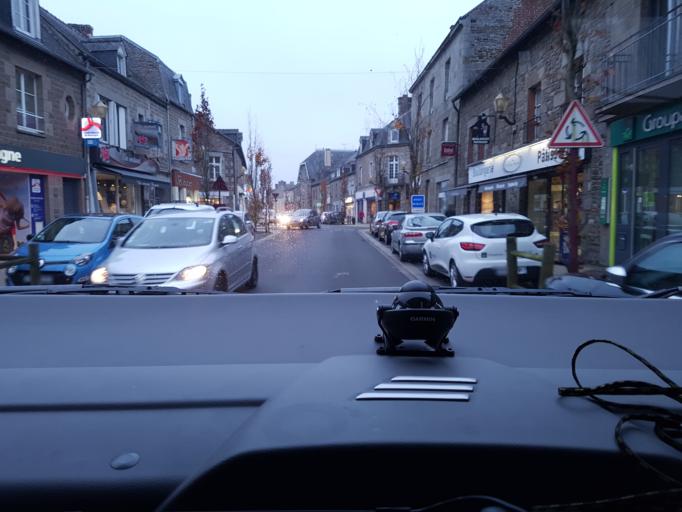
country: FR
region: Brittany
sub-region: Departement d'Ille-et-Vilaine
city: Saint-Brice-en-Cogles
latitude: 48.4109
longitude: -1.3664
